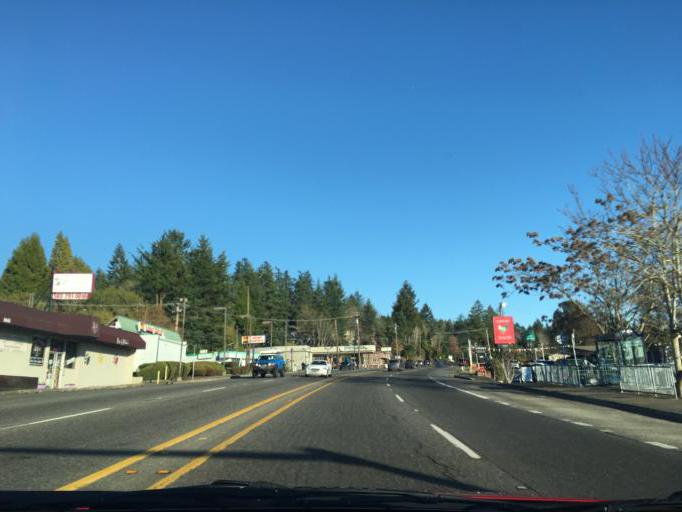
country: US
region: Oregon
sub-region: Washington County
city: West Slope
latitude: 45.4980
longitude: -122.7668
